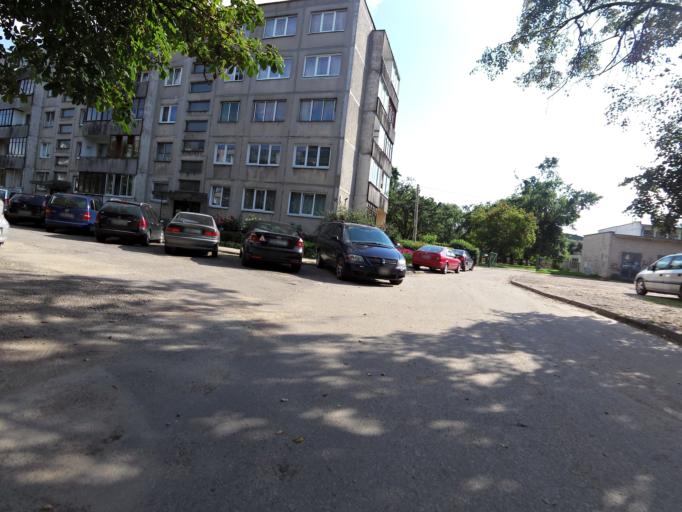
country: LT
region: Vilnius County
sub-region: Vilnius
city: Vilnius
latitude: 54.7030
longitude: 25.2957
